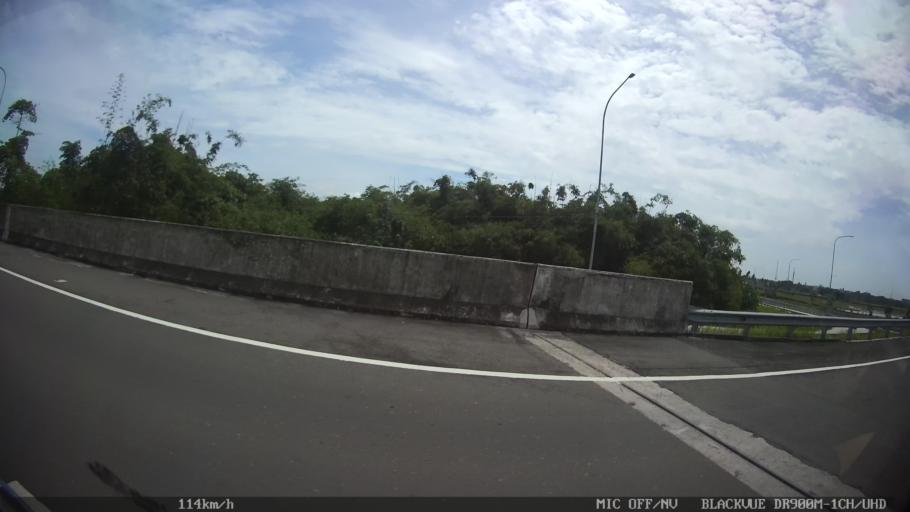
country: ID
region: North Sumatra
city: Percut
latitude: 3.5624
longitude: 98.8505
